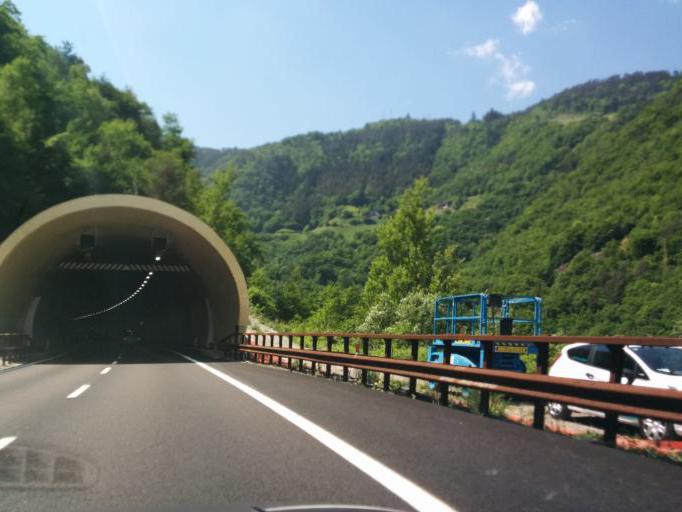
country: IT
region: Trentino-Alto Adige
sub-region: Bolzano
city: Ponte Gardena
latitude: 46.5621
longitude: 11.5146
